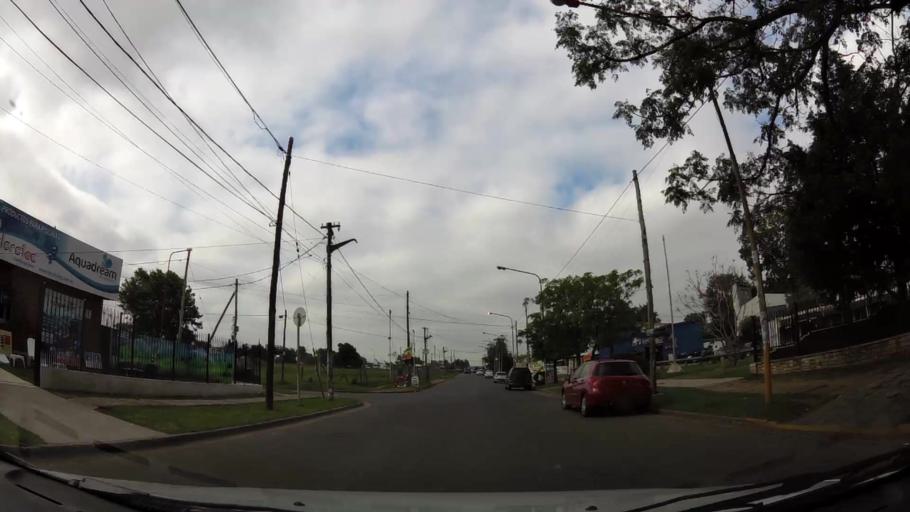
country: AR
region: Buenos Aires
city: San Justo
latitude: -34.7262
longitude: -58.5334
